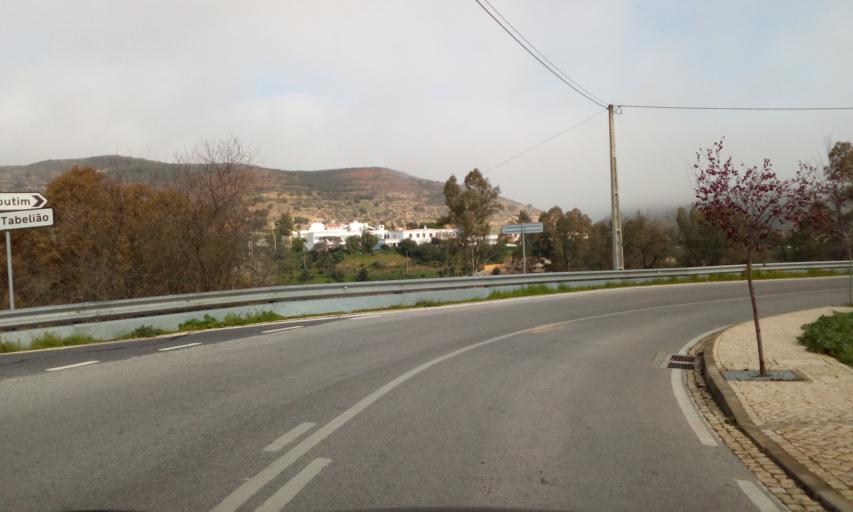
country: PT
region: Faro
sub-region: Alcoutim
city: Alcoutim
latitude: 37.4704
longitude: -7.4769
